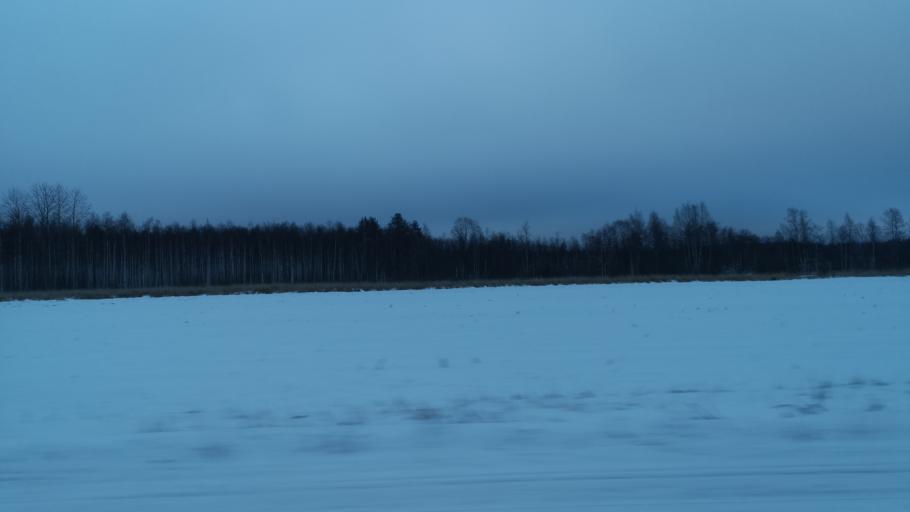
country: FI
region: Southern Savonia
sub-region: Savonlinna
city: Enonkoski
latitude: 62.0835
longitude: 28.6951
